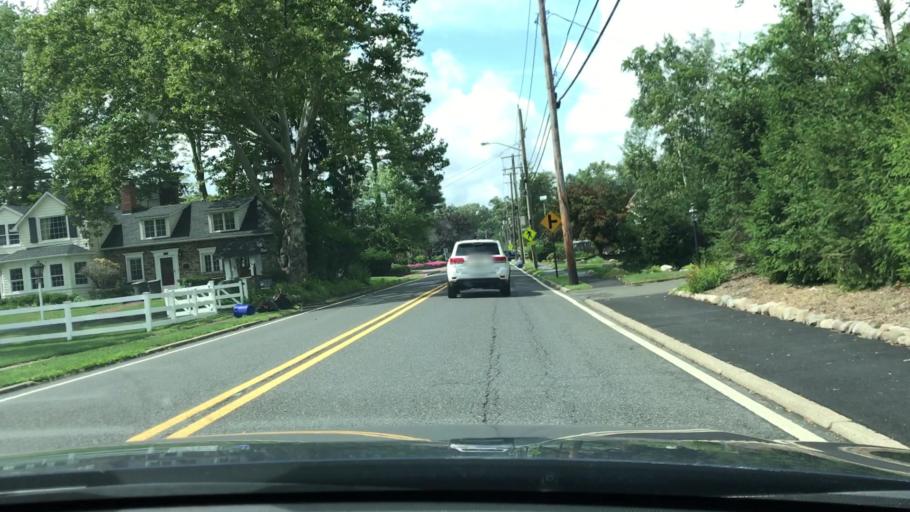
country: US
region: New Jersey
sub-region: Bergen County
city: Wyckoff
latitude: 41.0043
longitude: -74.1588
